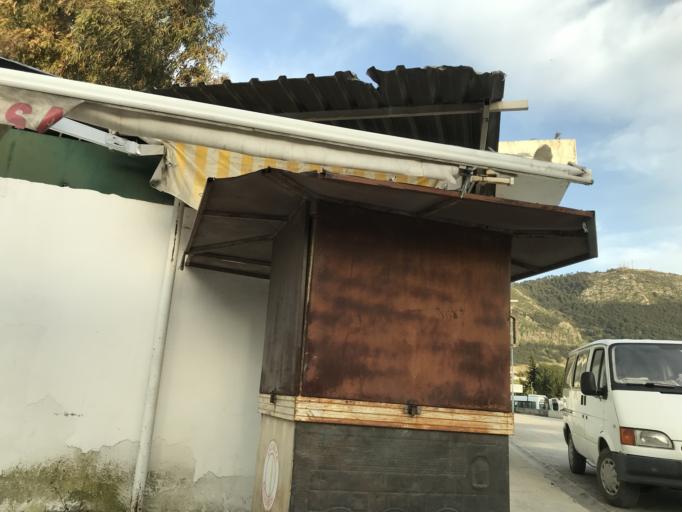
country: TR
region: Hatay
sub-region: Antakya Ilcesi
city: Antakya
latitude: 36.2122
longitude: 36.1657
